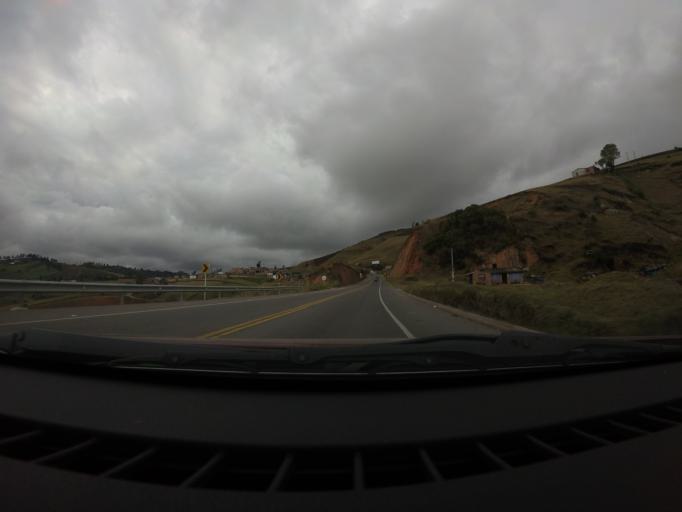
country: CO
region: Boyaca
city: Tunja
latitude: 5.4991
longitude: -73.3805
